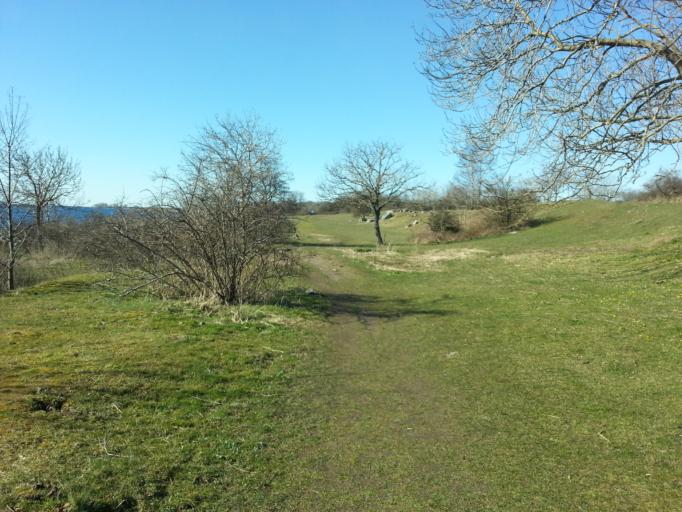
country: SE
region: Skane
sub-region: Simrishamns Kommun
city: Simrishamn
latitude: 55.5076
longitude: 14.3419
